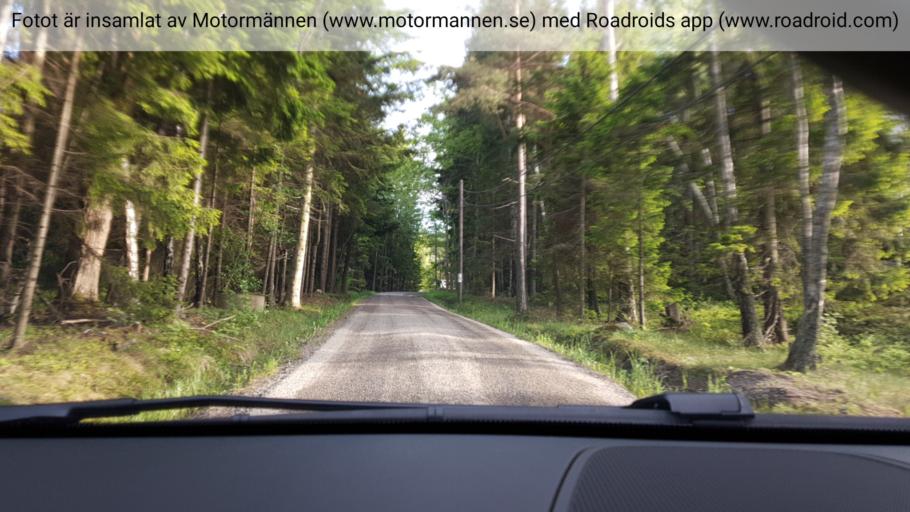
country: SE
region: Stockholm
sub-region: Haninge Kommun
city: Jordbro
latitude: 59.0184
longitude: 18.1090
